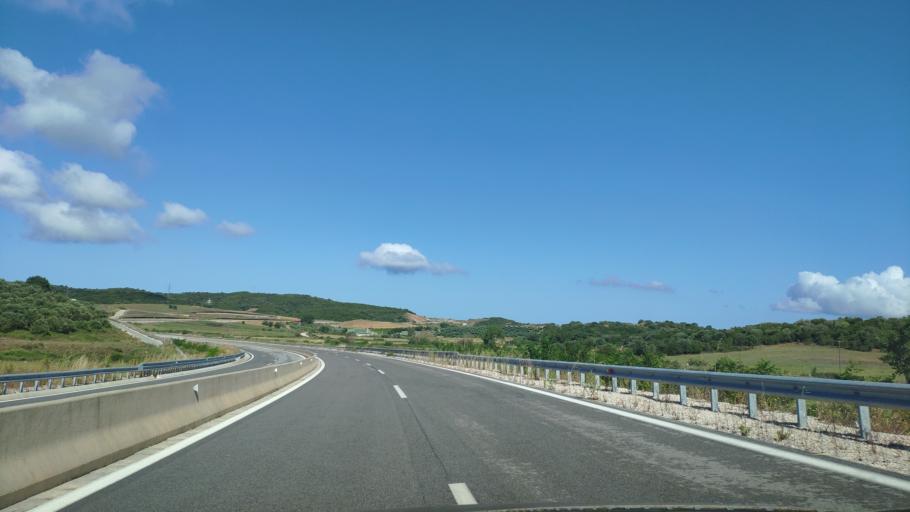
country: GR
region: West Greece
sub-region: Nomos Aitolias kai Akarnanias
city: Vonitsa
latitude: 38.9114
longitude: 20.8429
